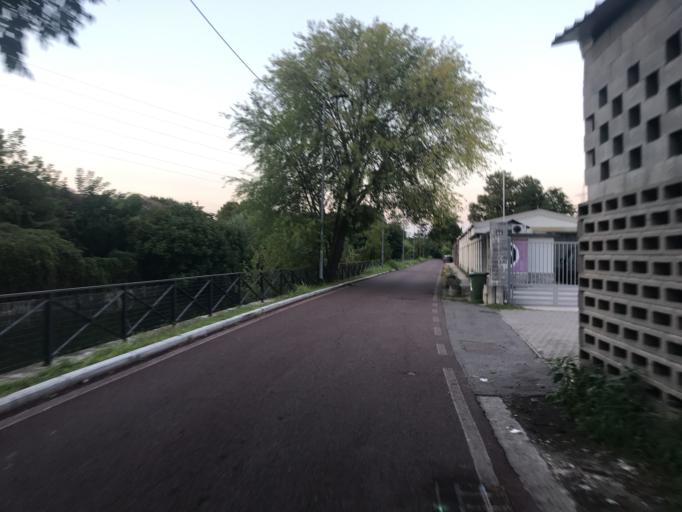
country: IT
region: Lombardy
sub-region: Citta metropolitana di Milano
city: Sesto San Giovanni
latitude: 45.5139
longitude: 9.2539
